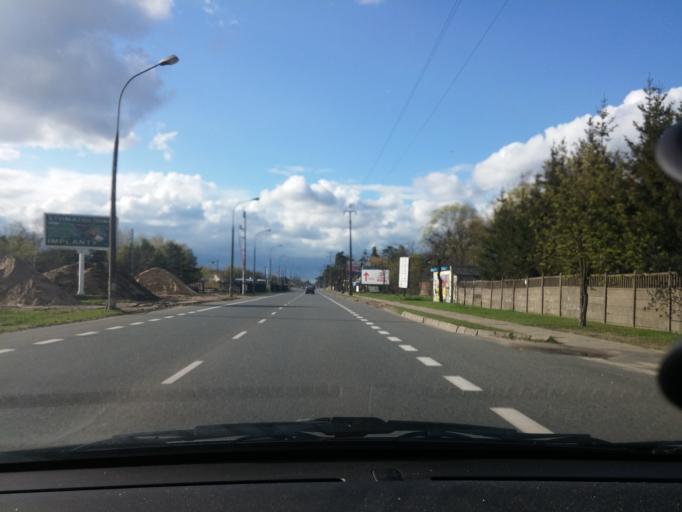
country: PL
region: Masovian Voivodeship
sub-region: Warszawa
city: Wawer
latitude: 52.1896
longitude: 21.1838
